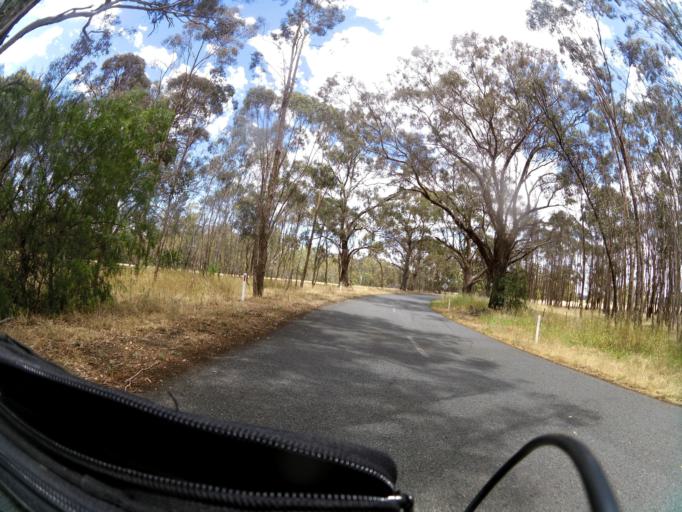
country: AU
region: Victoria
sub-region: Greater Shepparton
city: Shepparton
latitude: -36.6475
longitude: 145.2099
